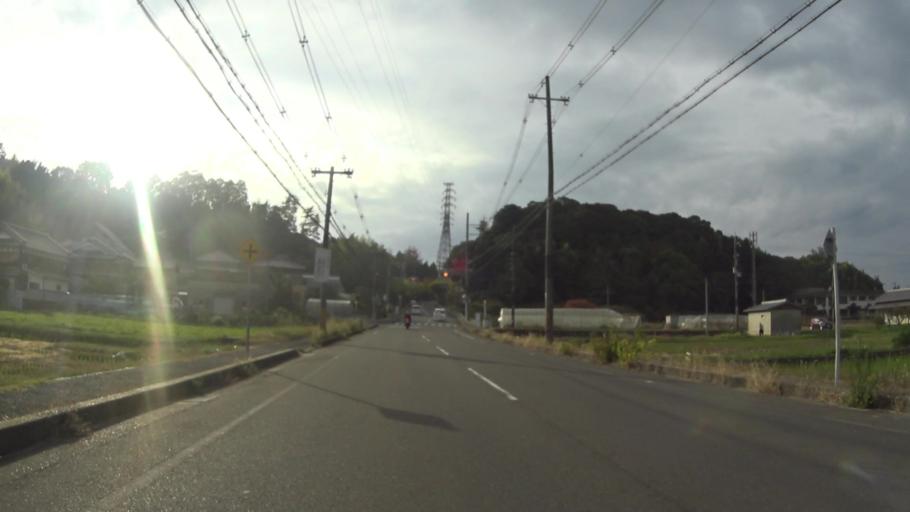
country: JP
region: Nara
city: Nara-shi
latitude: 34.7311
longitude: 135.7978
